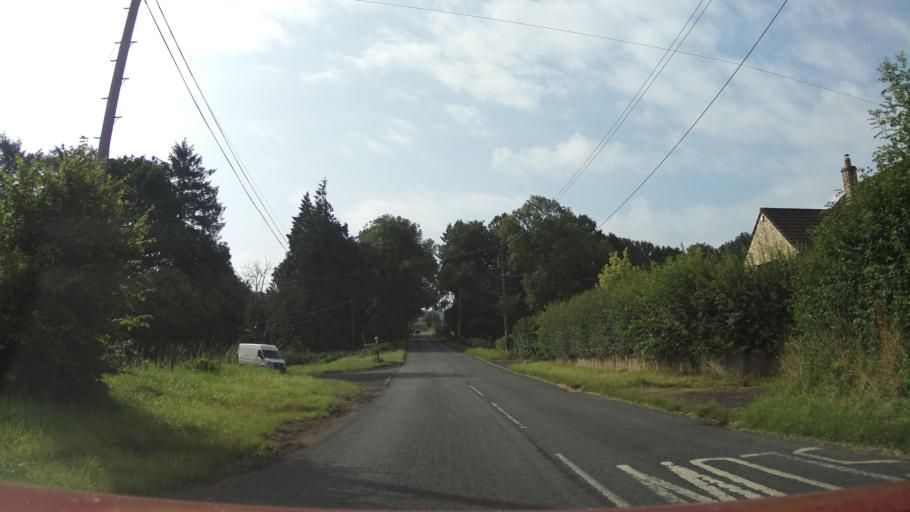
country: GB
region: England
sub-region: Bath and North East Somerset
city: East Harptree
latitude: 51.2989
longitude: -2.6019
